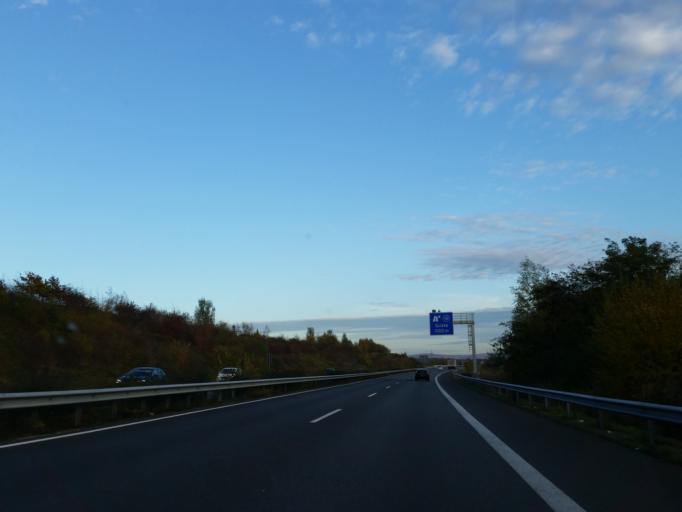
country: DE
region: Lower Saxony
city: Braunschweig
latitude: 52.2509
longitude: 10.5796
